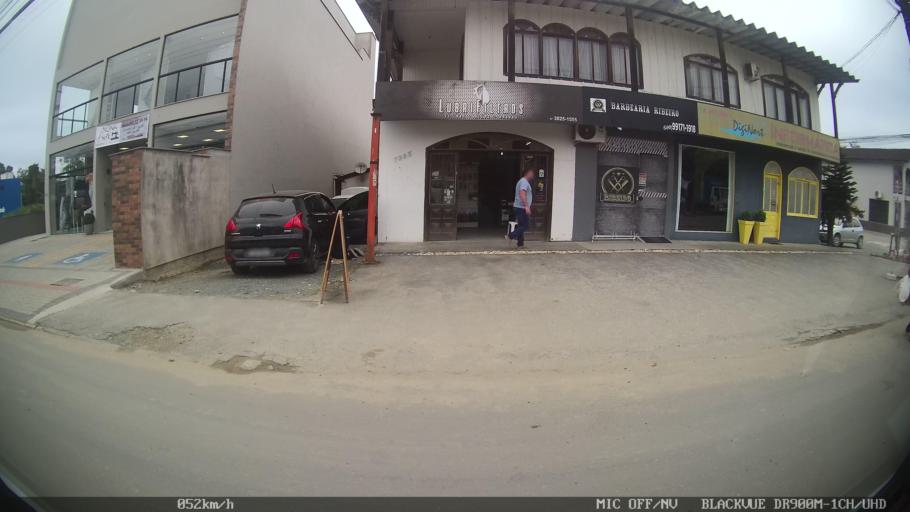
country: BR
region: Santa Catarina
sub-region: Joinville
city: Joinville
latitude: -26.2872
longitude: -48.9133
